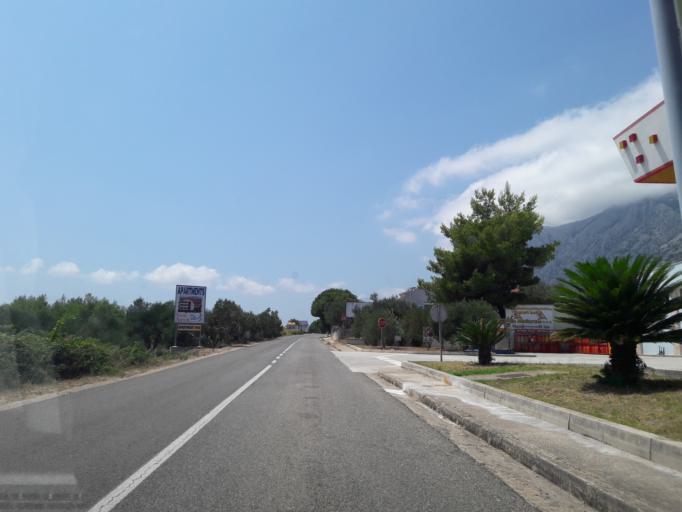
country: HR
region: Dubrovacko-Neretvanska
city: Orebic
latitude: 42.9837
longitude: 17.2005
